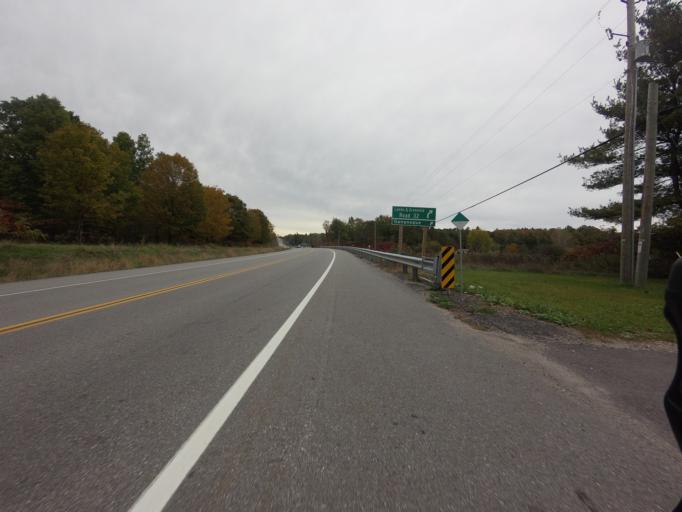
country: CA
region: Ontario
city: Gananoque
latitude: 44.4828
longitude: -76.1974
